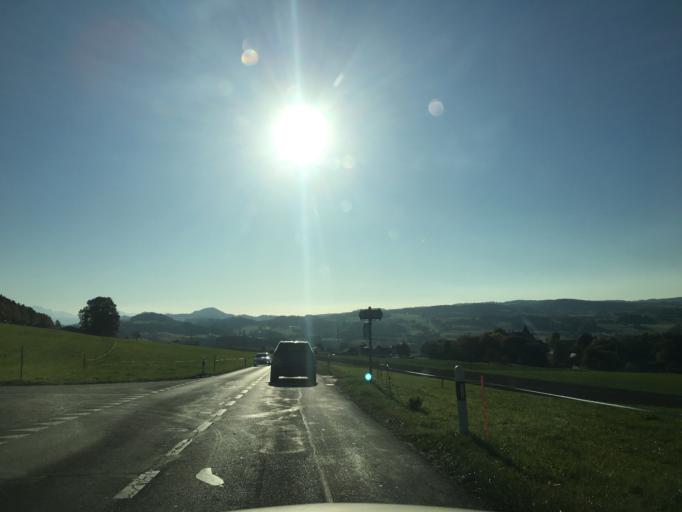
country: CH
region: Vaud
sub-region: Lavaux-Oron District
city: Oron-la-ville
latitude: 46.5767
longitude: 6.8497
